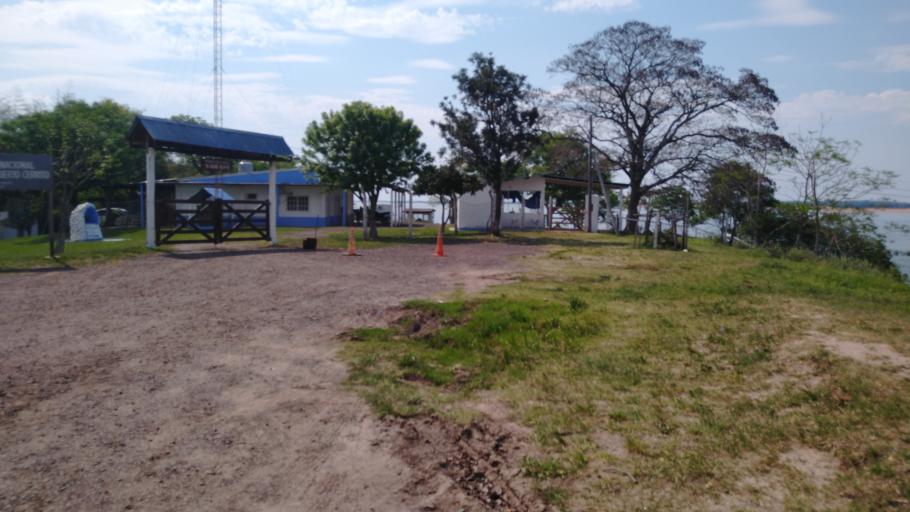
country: PY
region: Neembucu
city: Cerrito
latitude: -27.3703
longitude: -57.6553
